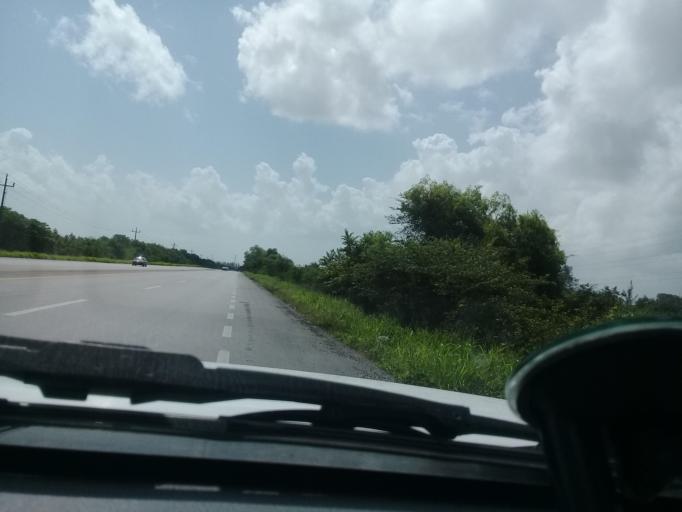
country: MX
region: Veracruz
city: Moralillo
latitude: 22.2130
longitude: -97.9710
